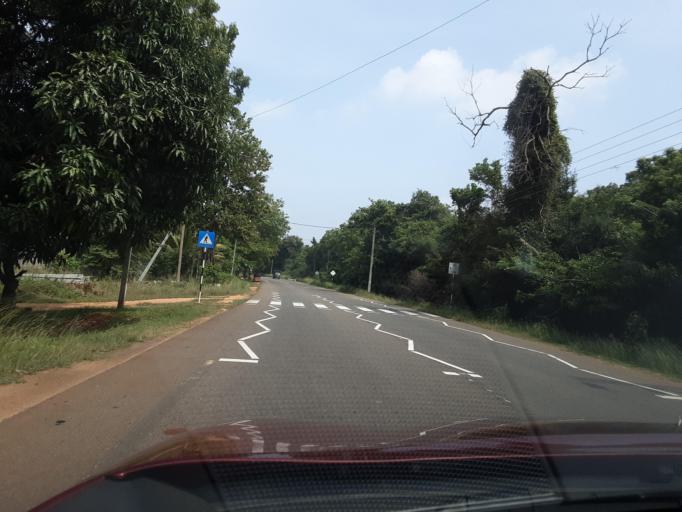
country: LK
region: North Central
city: Anuradhapura
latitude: 8.3424
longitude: 80.5047
